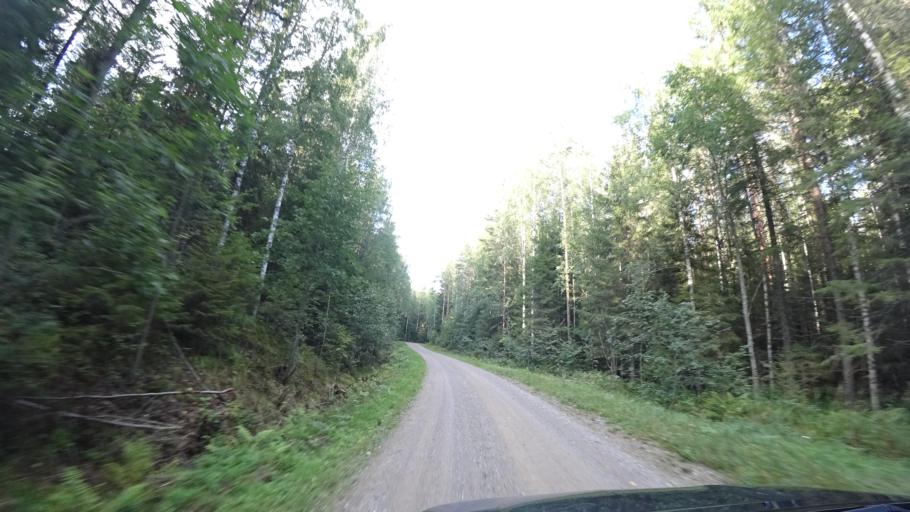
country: FI
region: Paijanne Tavastia
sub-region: Lahti
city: Auttoinen
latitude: 61.2187
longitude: 25.1789
